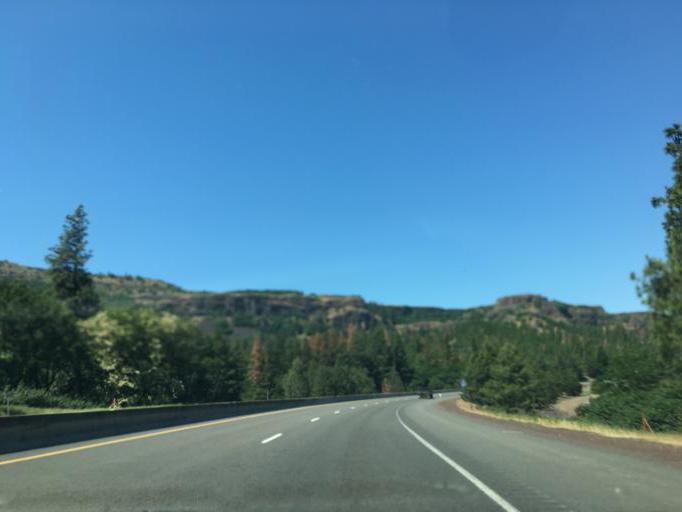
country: US
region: Oregon
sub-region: Wasco County
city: Chenoweth
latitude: 45.6769
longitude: -121.2850
